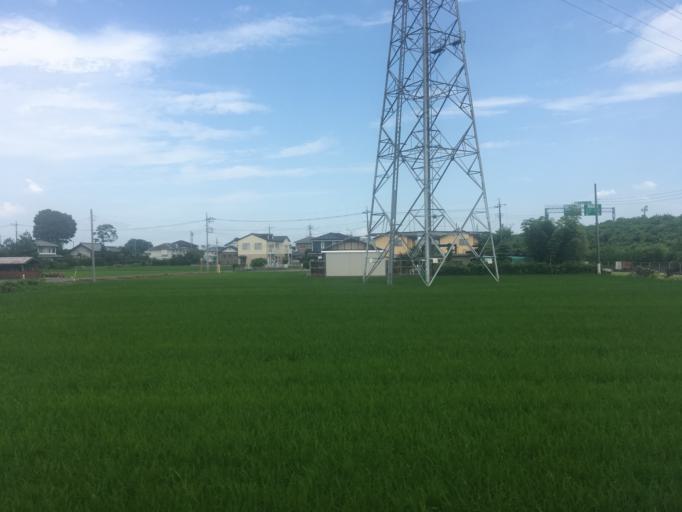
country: JP
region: Gunma
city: Fujioka
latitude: 36.2740
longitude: 139.0838
